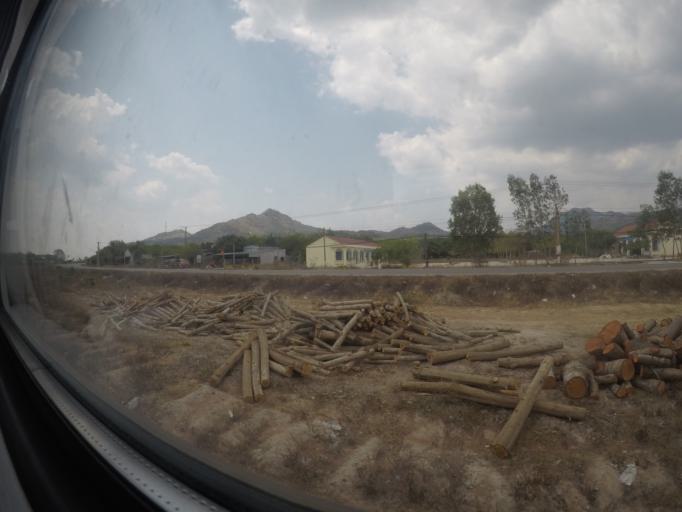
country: VN
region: Binh Thuan
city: Tanh Linh
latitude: 10.9643
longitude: 107.6370
